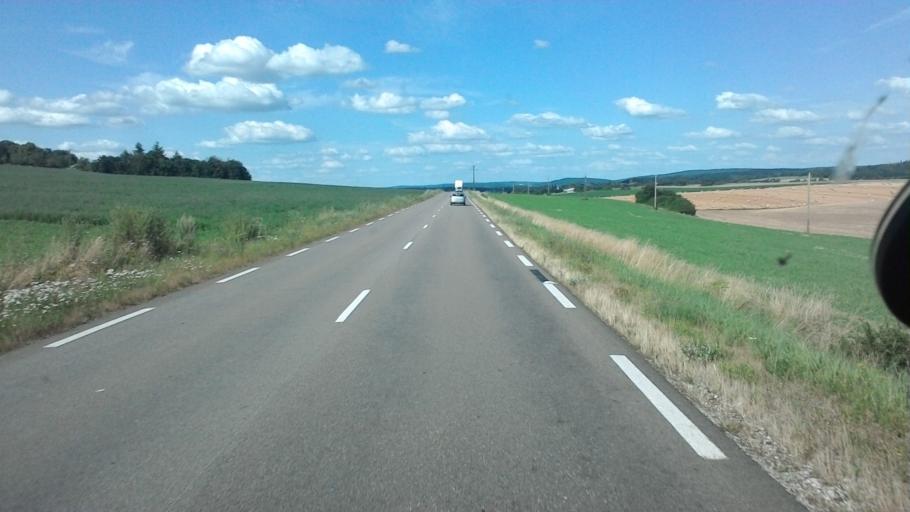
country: FR
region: Franche-Comte
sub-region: Departement de la Haute-Saone
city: Gy
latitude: 47.4732
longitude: 5.9263
